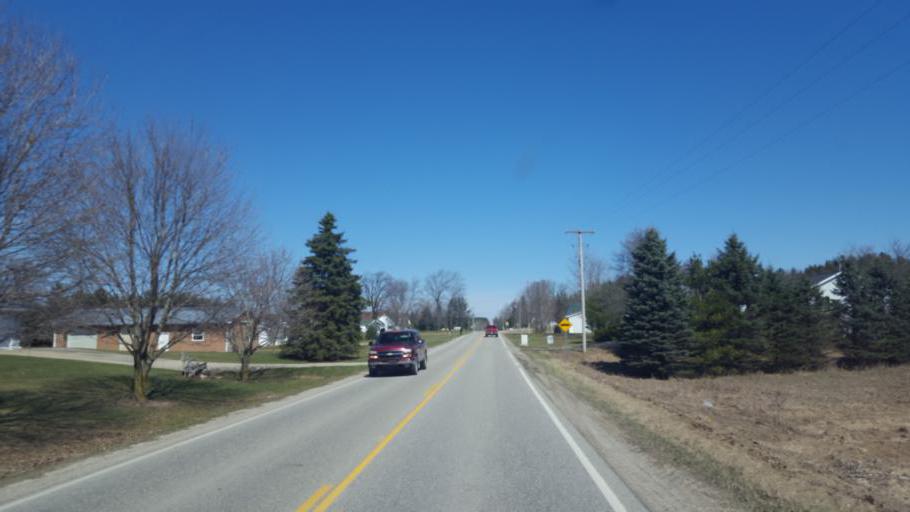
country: US
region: Michigan
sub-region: Montcalm County
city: Edmore
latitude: 43.5170
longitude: -85.0853
